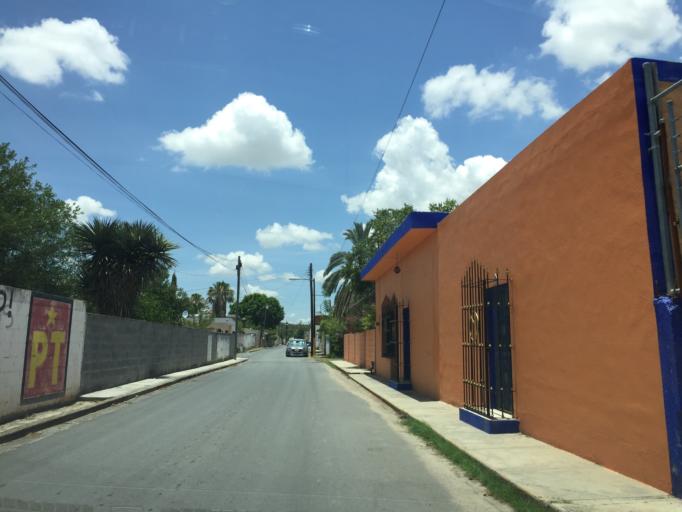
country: MX
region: Nuevo Leon
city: Marin
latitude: 25.8608
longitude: -99.9447
